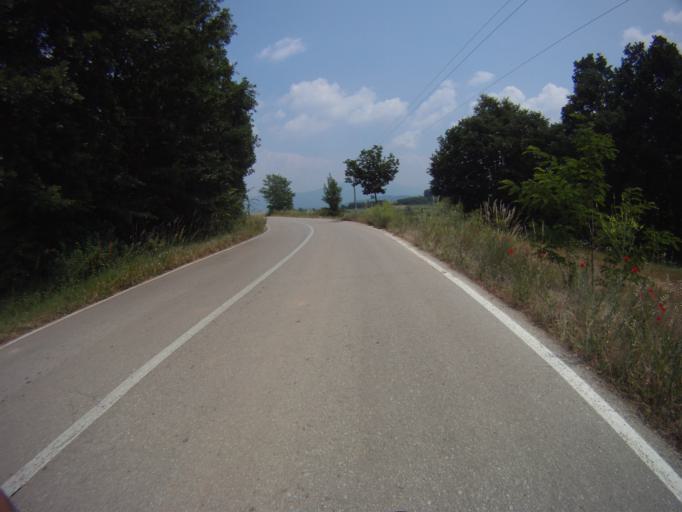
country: RS
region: Central Serbia
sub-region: Nisavski Okrug
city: Gadzin Han
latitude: 43.2023
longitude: 21.9795
